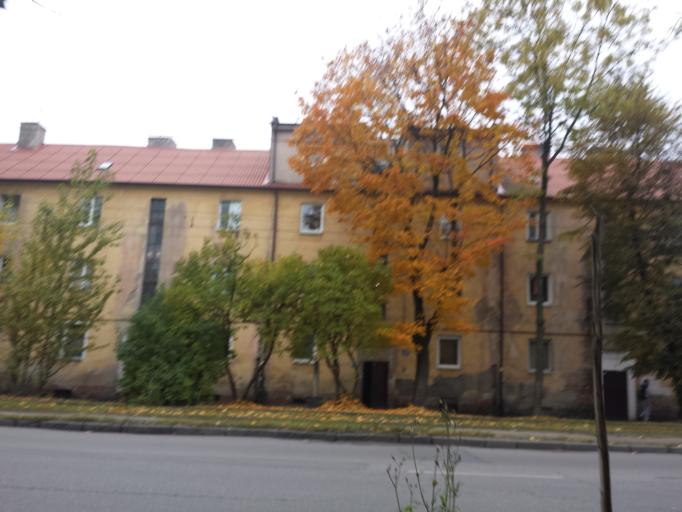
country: RU
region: Kaliningrad
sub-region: Gorod Kaliningrad
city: Kaliningrad
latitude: 54.6903
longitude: 20.5235
